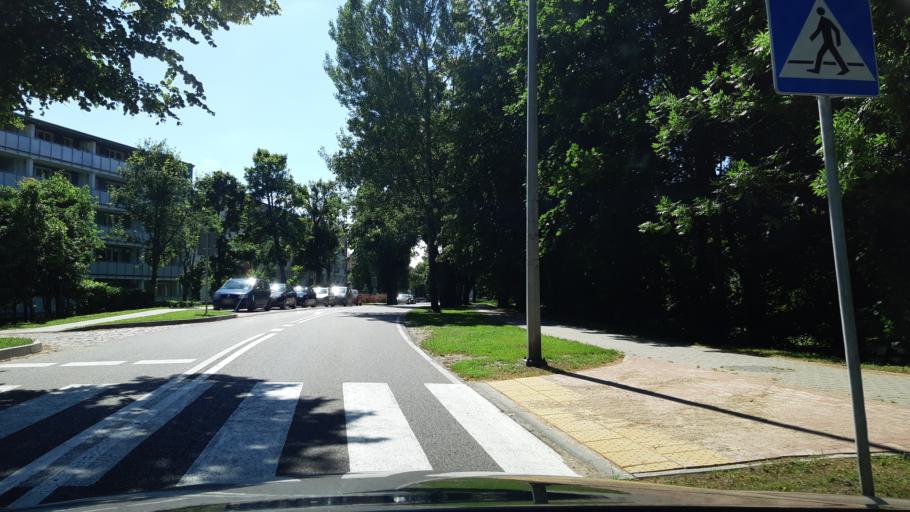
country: PL
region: Warmian-Masurian Voivodeship
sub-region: Powiat gizycki
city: Gizycko
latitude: 54.0367
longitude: 21.7523
